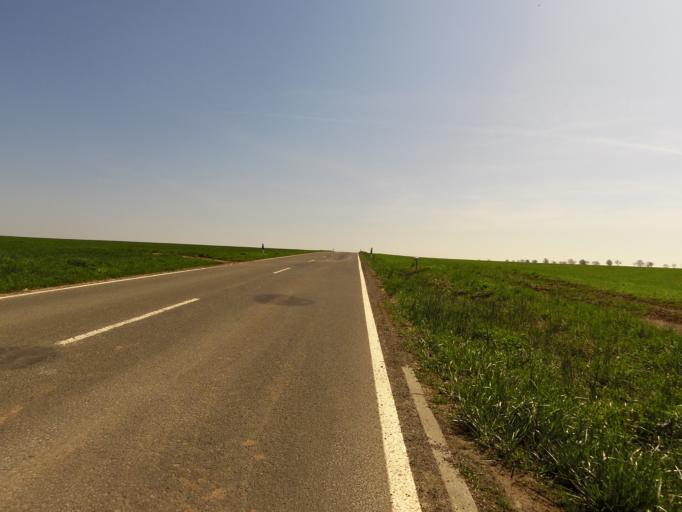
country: DE
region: Rheinland-Pfalz
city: Lautersheim
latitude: 49.5901
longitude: 8.0777
